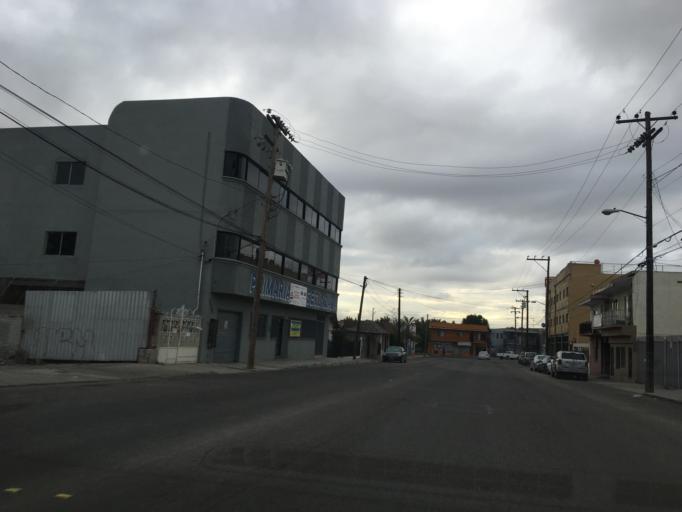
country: MX
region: Baja California
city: Tijuana
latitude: 32.5367
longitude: -117.0524
